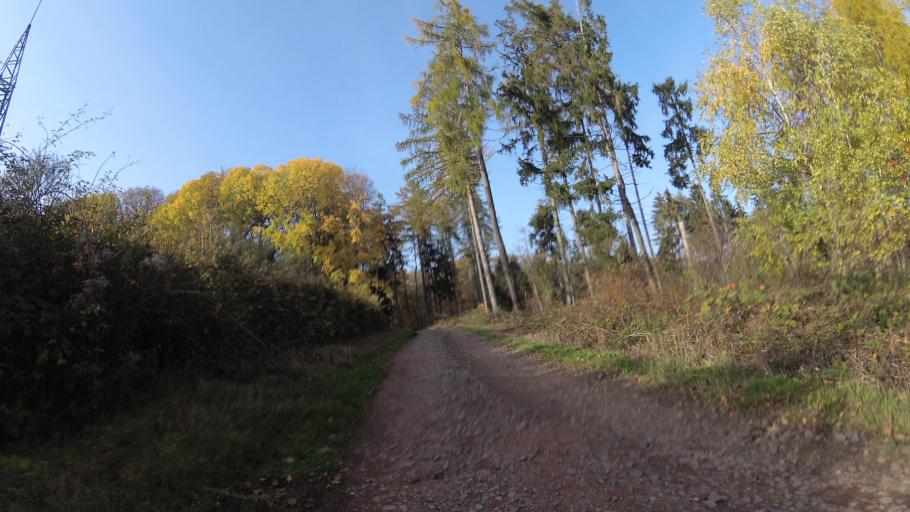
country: DE
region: Saarland
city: Hangard
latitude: 49.3705
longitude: 7.2362
